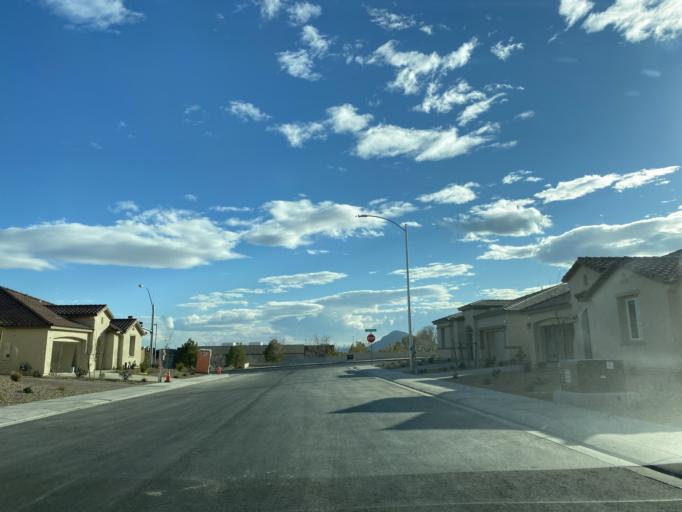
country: US
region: Nevada
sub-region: Clark County
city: Summerlin South
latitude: 36.2834
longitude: -115.3053
